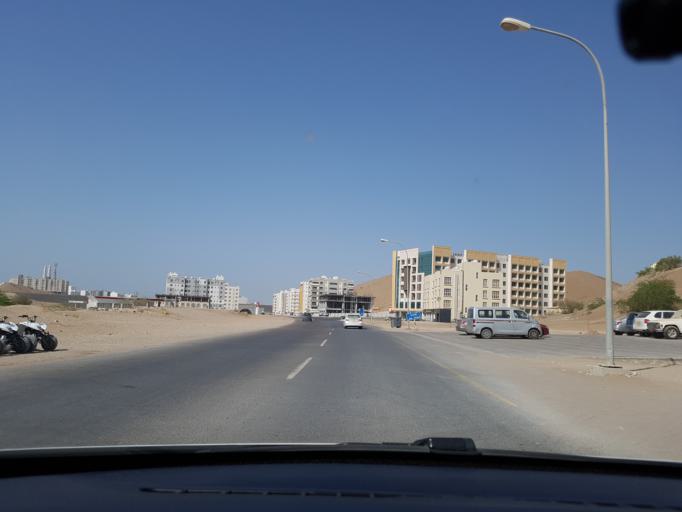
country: OM
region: Muhafazat Masqat
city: Bawshar
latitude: 23.5640
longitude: 58.4121
